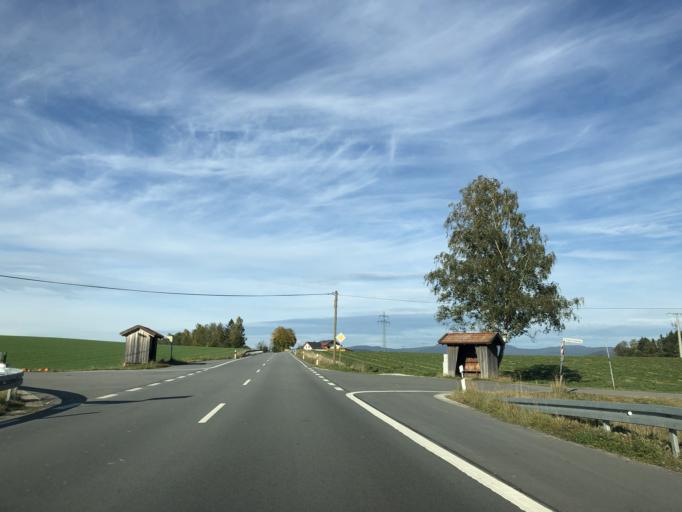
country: DE
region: Bavaria
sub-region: Lower Bavaria
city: Ruhmannsfelden
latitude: 48.9941
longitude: 12.9808
